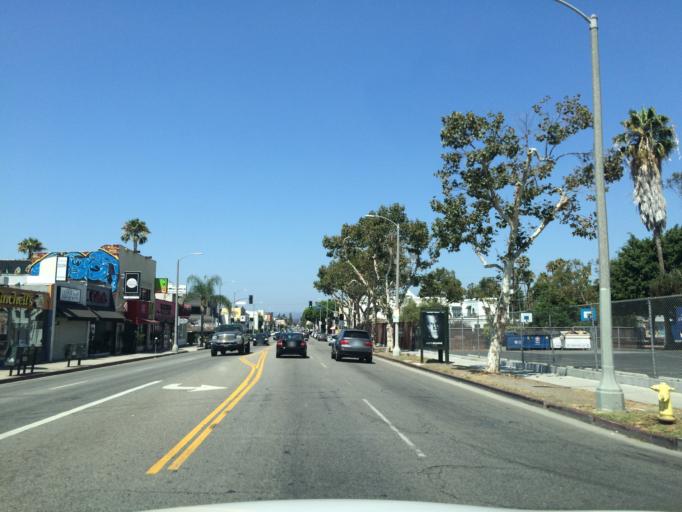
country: US
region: California
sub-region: Los Angeles County
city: West Hollywood
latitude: 34.0835
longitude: -118.3451
